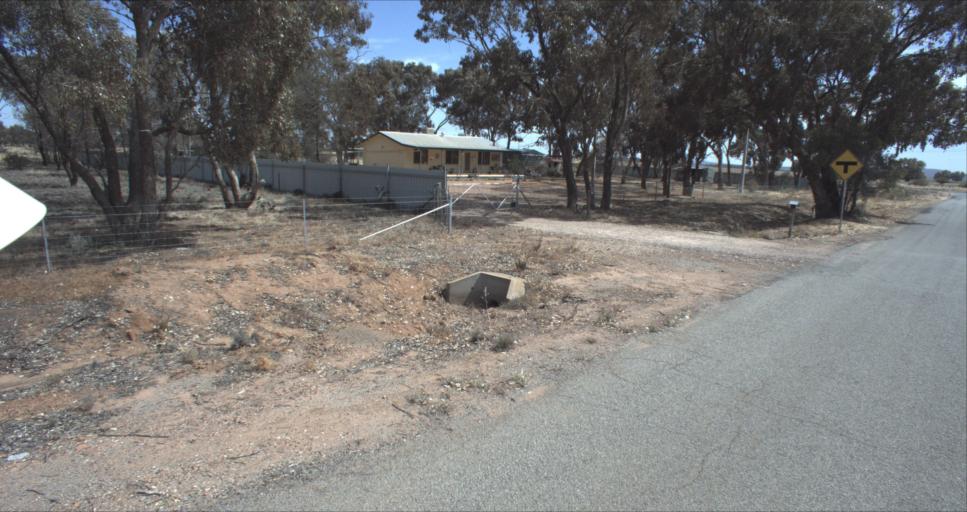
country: AU
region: New South Wales
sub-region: Leeton
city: Leeton
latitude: -34.5589
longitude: 146.4583
